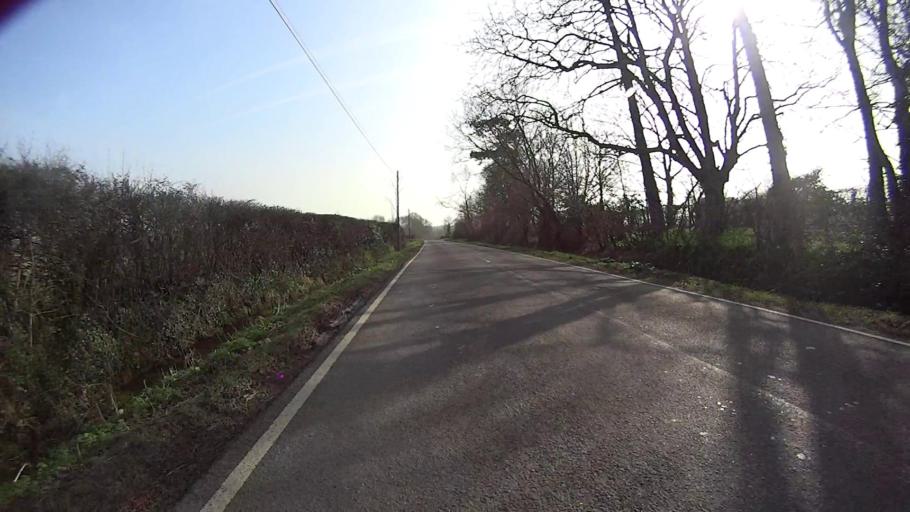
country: GB
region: England
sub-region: Surrey
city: Salfords
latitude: 51.2112
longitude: -0.1536
